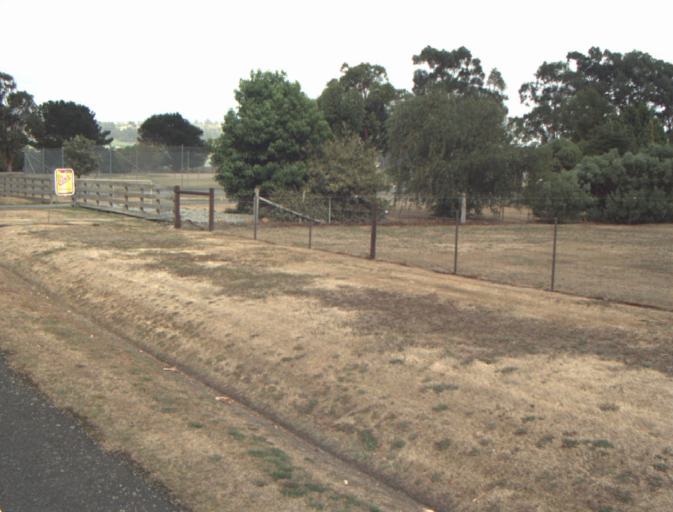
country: AU
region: Tasmania
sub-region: Launceston
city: Mayfield
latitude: -41.3313
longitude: 147.0558
